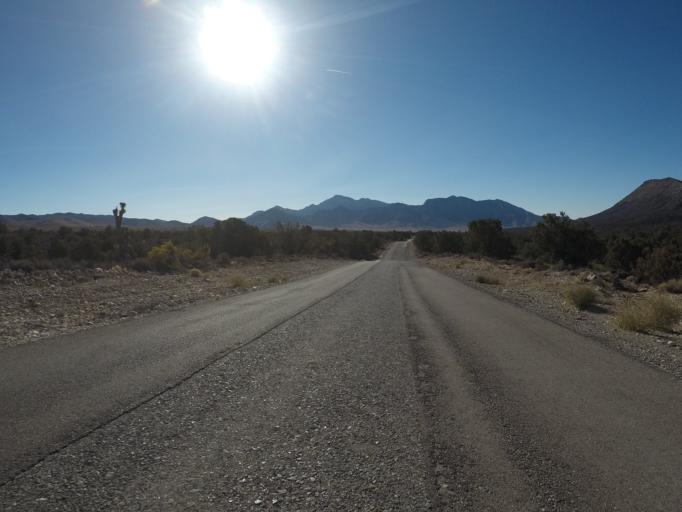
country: US
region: Nevada
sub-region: Clark County
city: Summerlin South
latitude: 36.0668
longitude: -115.5611
